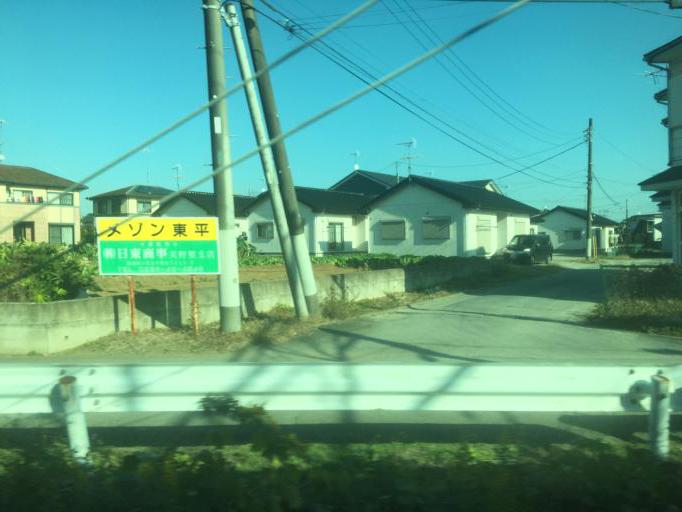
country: JP
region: Ibaraki
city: Ishioka
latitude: 36.2507
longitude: 140.2860
